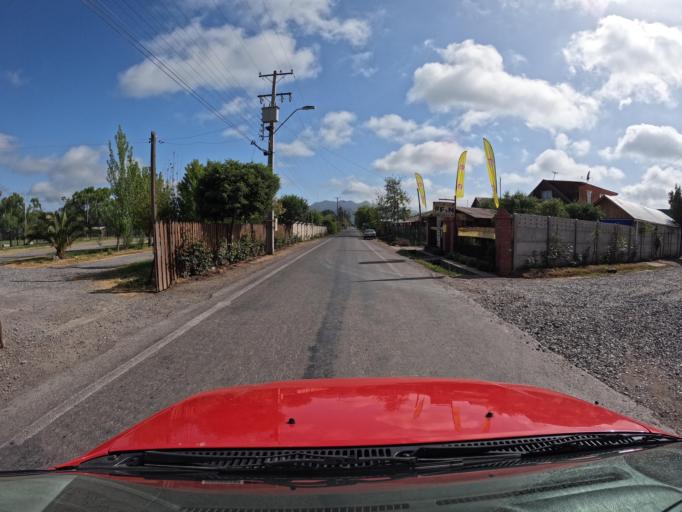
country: CL
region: Maule
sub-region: Provincia de Curico
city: Teno
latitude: -34.8785
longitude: -71.2258
